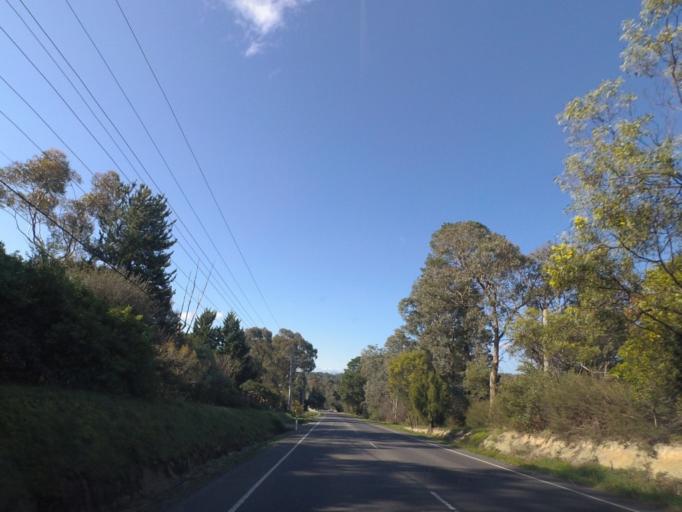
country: AU
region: Victoria
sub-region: Manningham
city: Park Orchards
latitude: -37.7701
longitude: 145.2234
